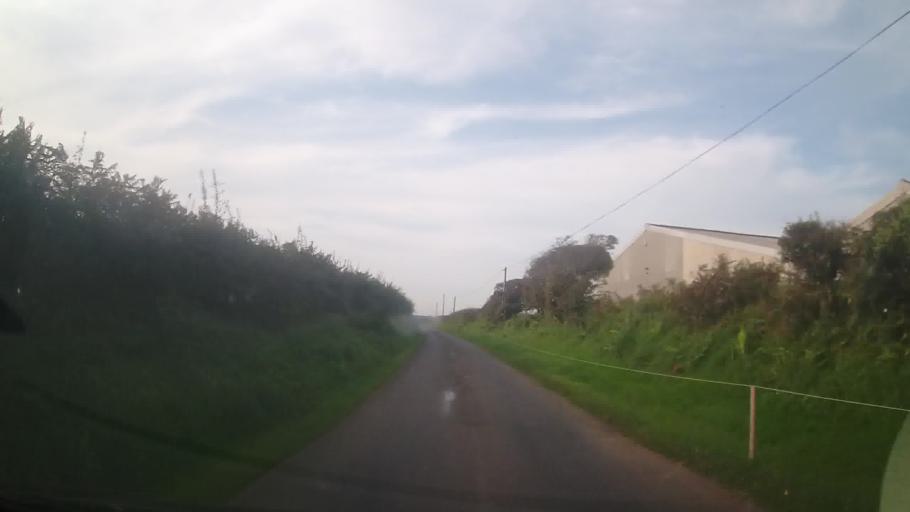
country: GB
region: Wales
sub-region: Pembrokeshire
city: Camrose
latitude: 51.8811
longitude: -5.0492
